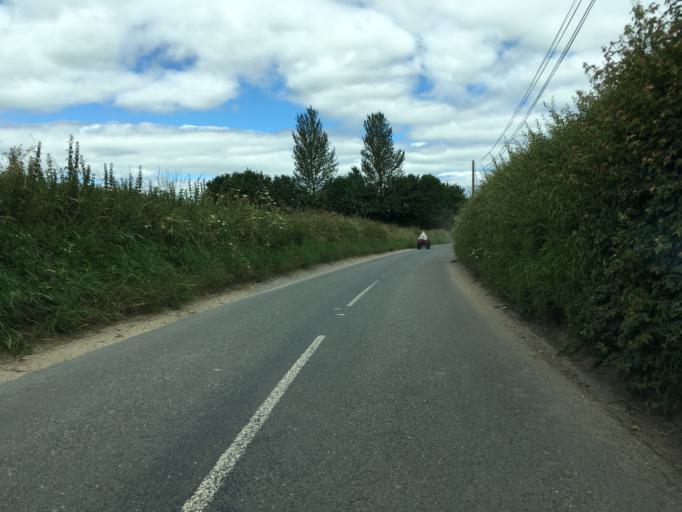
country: GB
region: England
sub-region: West Berkshire
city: Wickham
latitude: 51.4632
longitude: -1.4316
